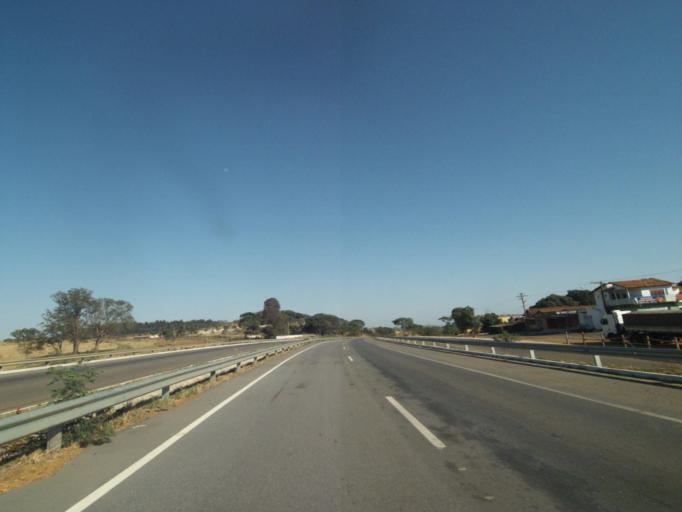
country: BR
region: Goias
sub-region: Anapolis
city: Anapolis
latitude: -16.1899
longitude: -49.0358
